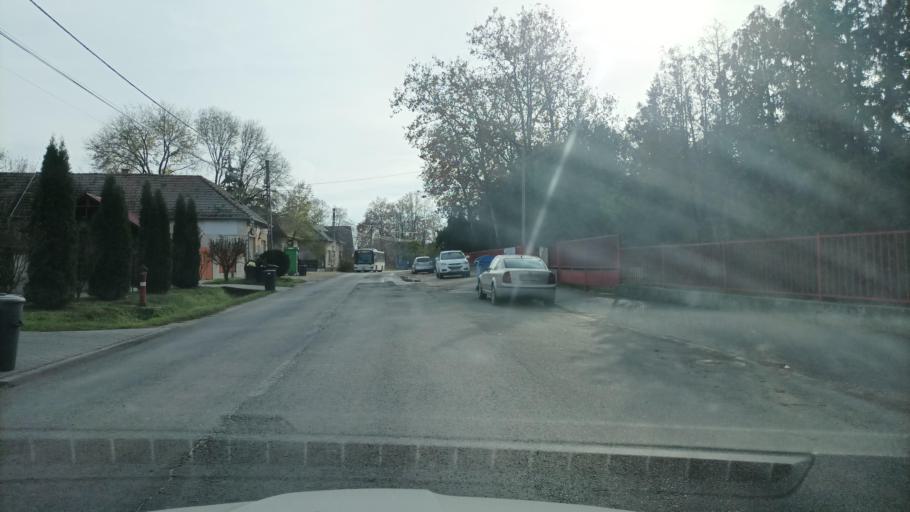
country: HU
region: Pest
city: Rackeve
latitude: 47.1338
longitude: 18.9476
